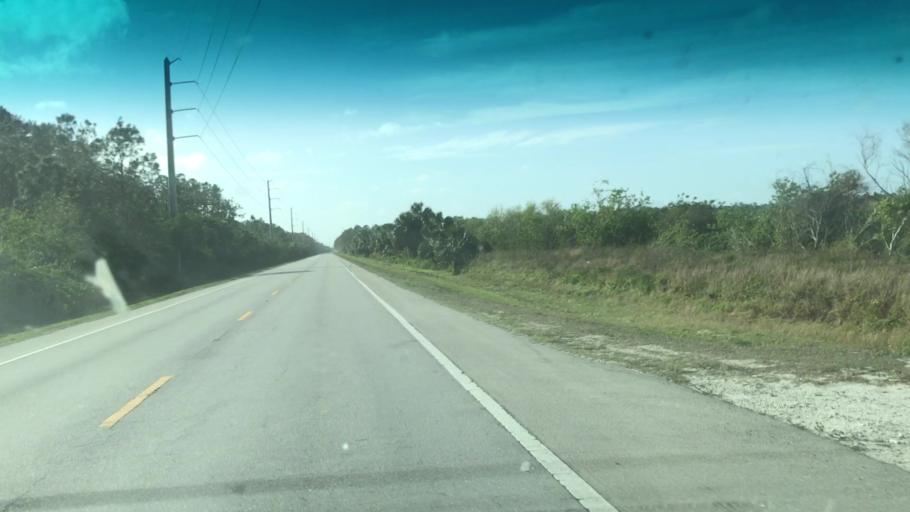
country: US
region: Florida
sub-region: Collier County
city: Orangetree
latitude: 26.3512
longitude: -81.5954
